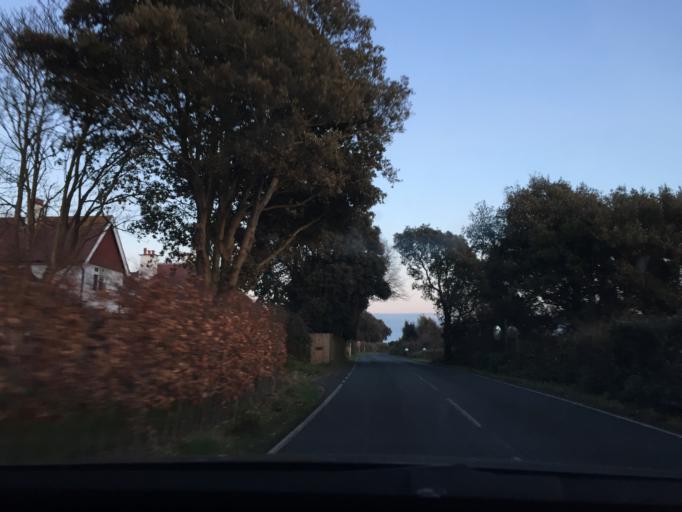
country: GB
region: England
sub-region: Hampshire
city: Gosport
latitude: 50.7811
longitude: -1.1453
